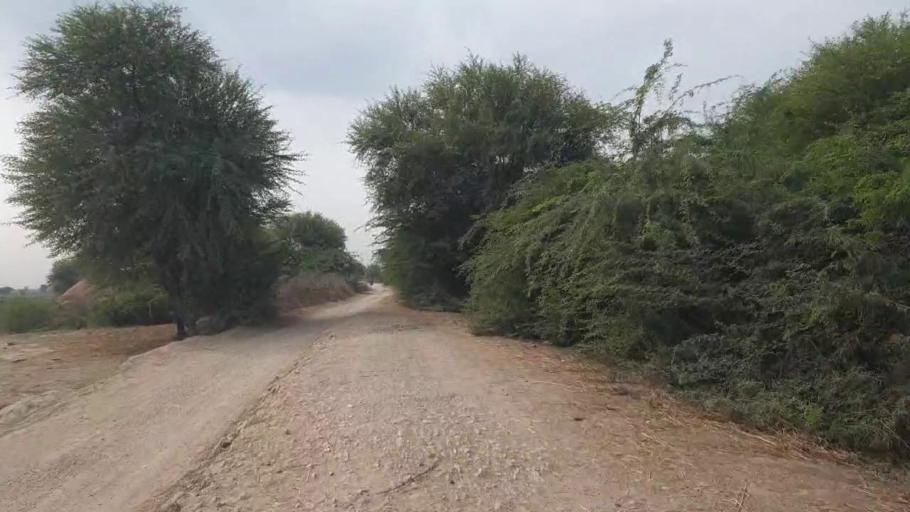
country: PK
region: Sindh
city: Talhar
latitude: 24.9164
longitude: 68.7760
